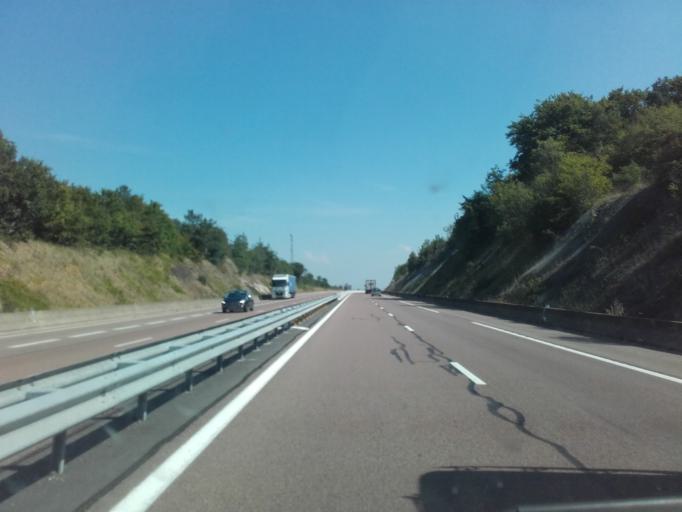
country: FR
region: Bourgogne
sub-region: Departement de la Cote-d'Or
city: Savigny-les-Beaune
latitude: 47.0876
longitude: 4.7567
